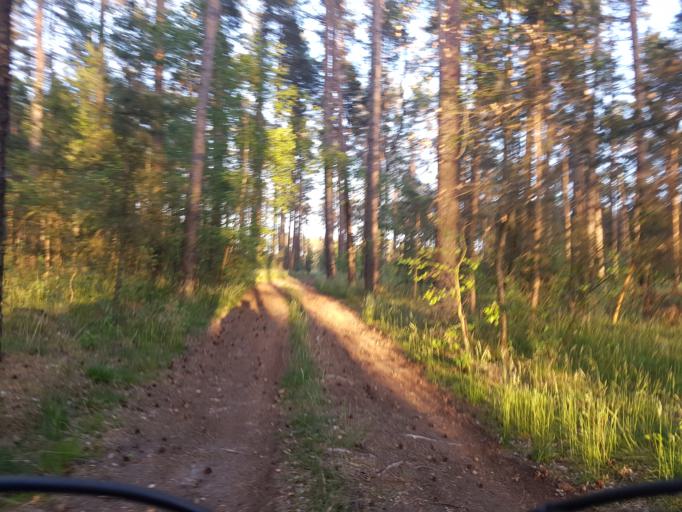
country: DE
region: Brandenburg
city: Schilda
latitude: 51.5600
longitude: 13.3765
